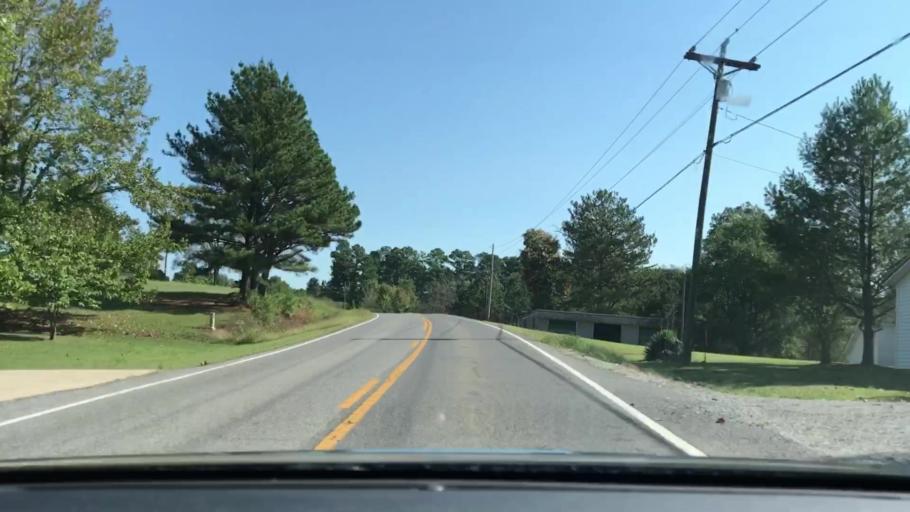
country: US
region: Kentucky
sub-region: Marshall County
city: Benton
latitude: 36.7669
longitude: -88.1826
